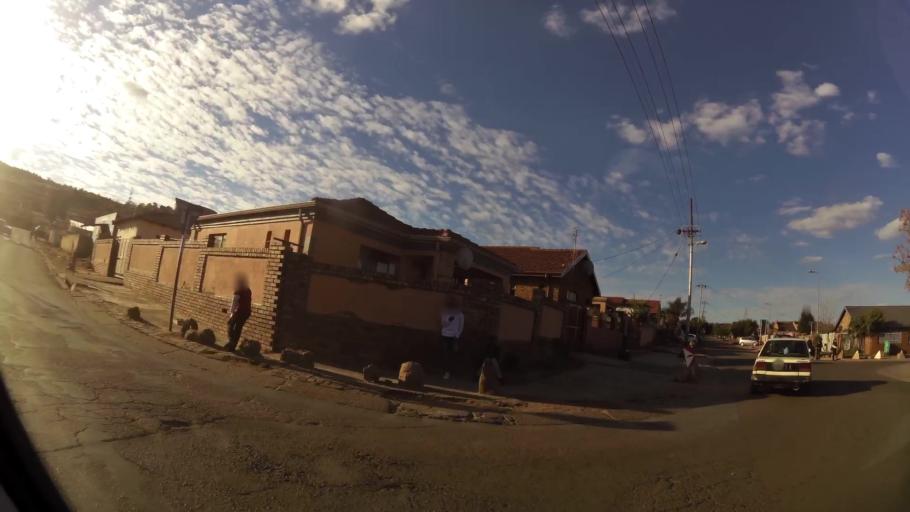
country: ZA
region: Gauteng
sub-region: City of Tshwane Metropolitan Municipality
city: Cullinan
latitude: -25.7051
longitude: 28.3850
